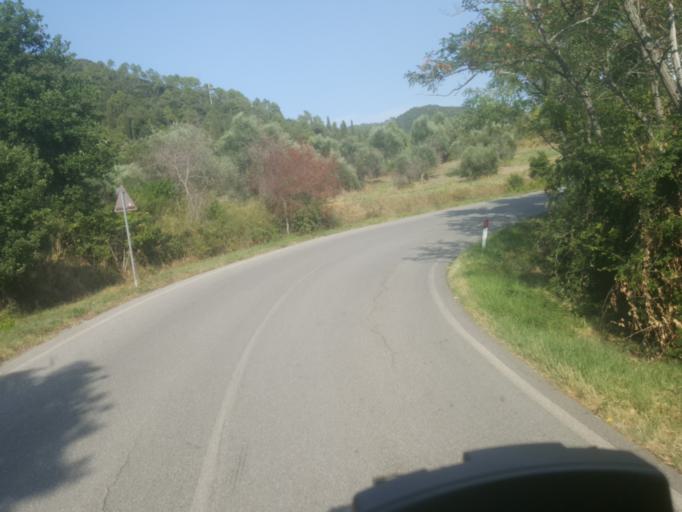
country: IT
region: Tuscany
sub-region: Province of Florence
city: Montaione
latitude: 43.4876
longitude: 10.8996
